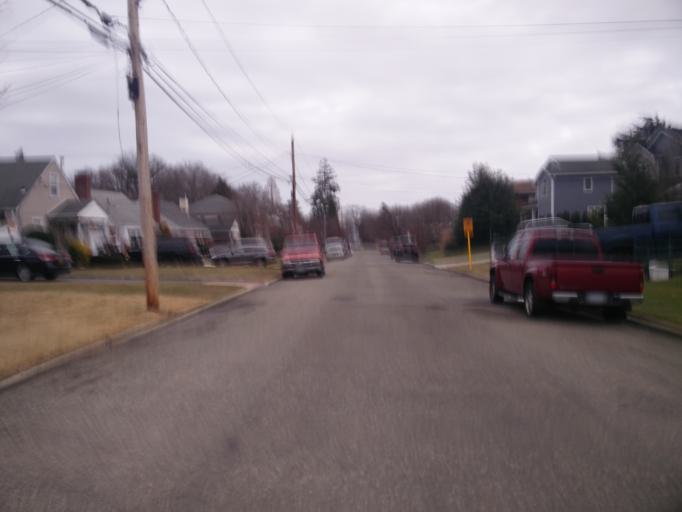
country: US
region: New York
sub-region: Nassau County
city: Glen Cove
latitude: 40.8704
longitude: -73.6436
